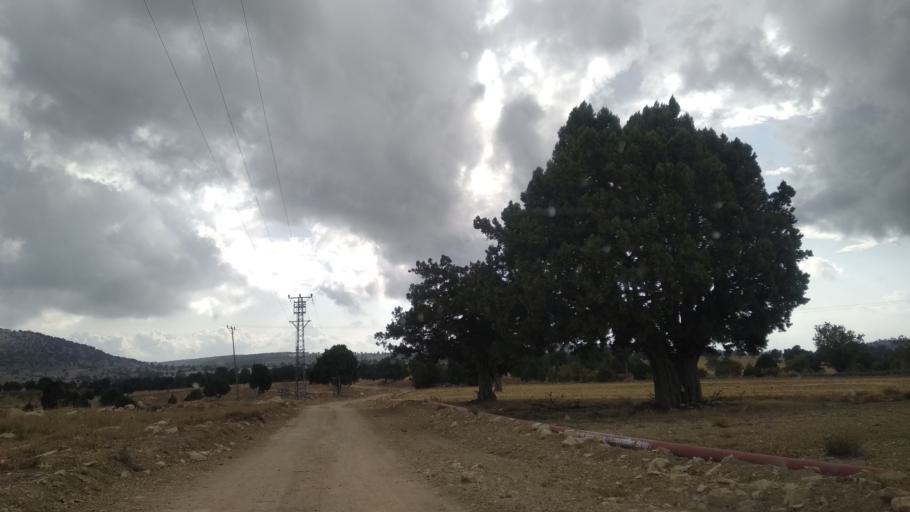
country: TR
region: Mersin
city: Sarikavak
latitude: 36.5709
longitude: 33.7471
